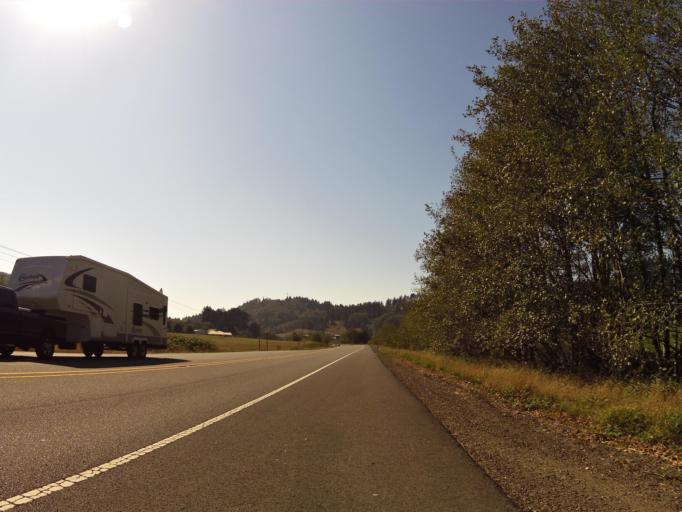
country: US
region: Oregon
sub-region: Tillamook County
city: Pacific City
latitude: 45.1600
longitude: -123.9437
